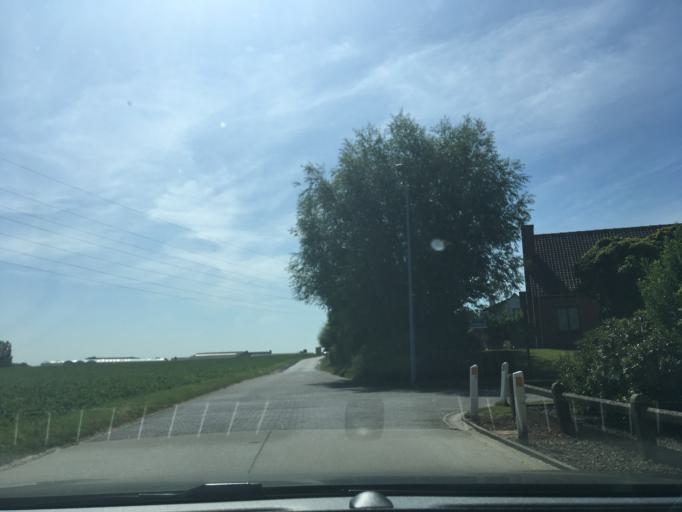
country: BE
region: Flanders
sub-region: Provincie West-Vlaanderen
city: Tielt
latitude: 50.9812
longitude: 3.3309
